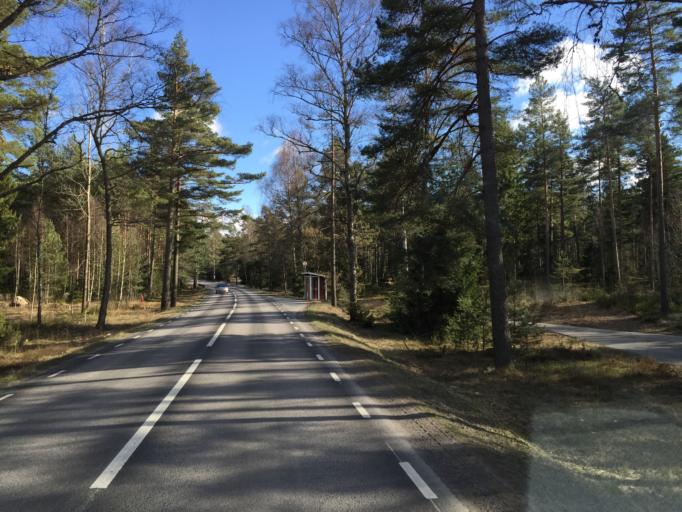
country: SE
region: Stockholm
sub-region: Sodertalje Kommun
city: Soedertaelje
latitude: 59.2337
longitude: 17.5479
